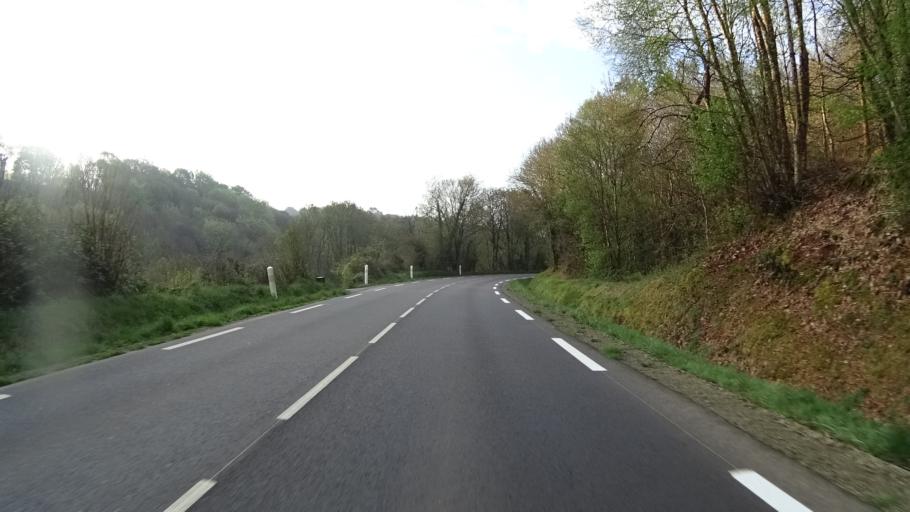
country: FR
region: Brittany
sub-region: Departement du Finistere
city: La Roche-Maurice
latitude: 48.4629
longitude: -4.1952
